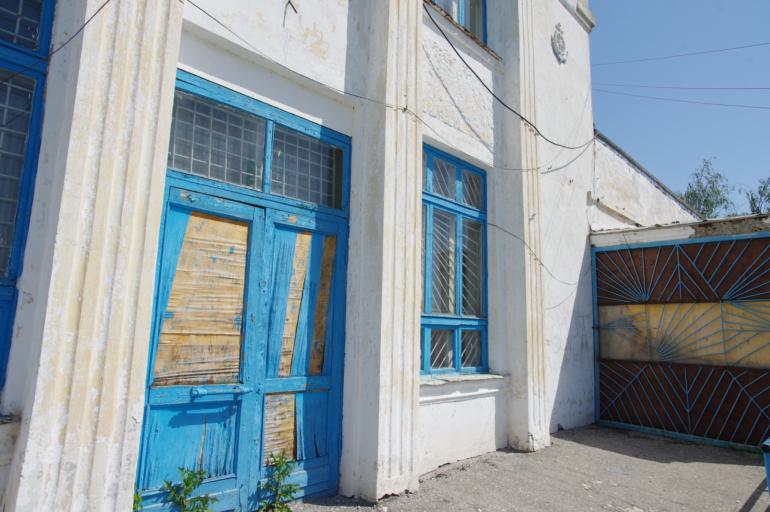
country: RU
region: Rjazan
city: Kasimov
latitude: 54.9389
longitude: 41.3782
